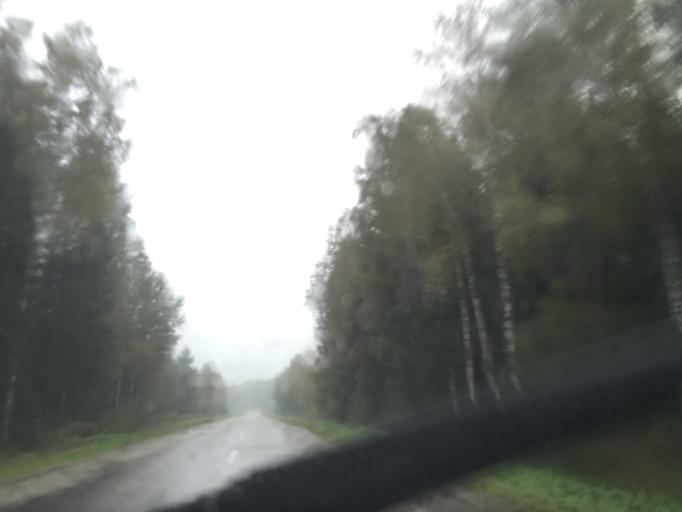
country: LV
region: Ropazu
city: Ropazi
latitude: 56.9982
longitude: 24.6604
